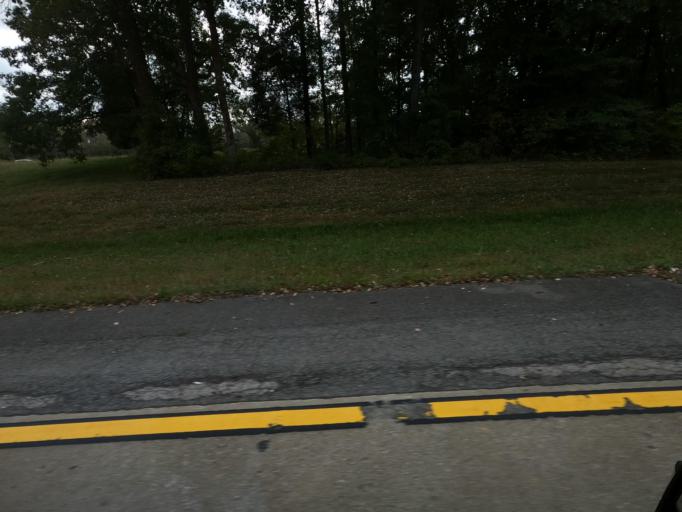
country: US
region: Tennessee
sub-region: Cheatham County
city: Pleasant View
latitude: 36.4500
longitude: -87.0971
